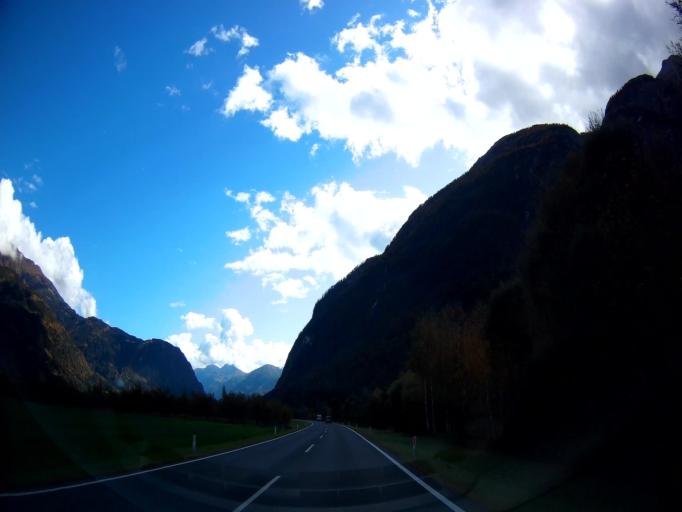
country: AT
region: Tyrol
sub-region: Politischer Bezirk Lienz
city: Nikolsdorf
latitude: 46.7870
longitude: 12.8795
